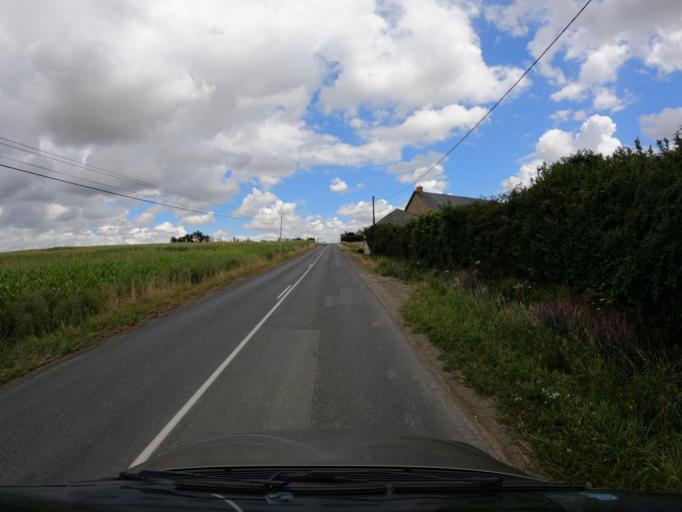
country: FR
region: Pays de la Loire
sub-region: Departement de Maine-et-Loire
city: Mire
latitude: 47.7828
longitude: -0.4582
